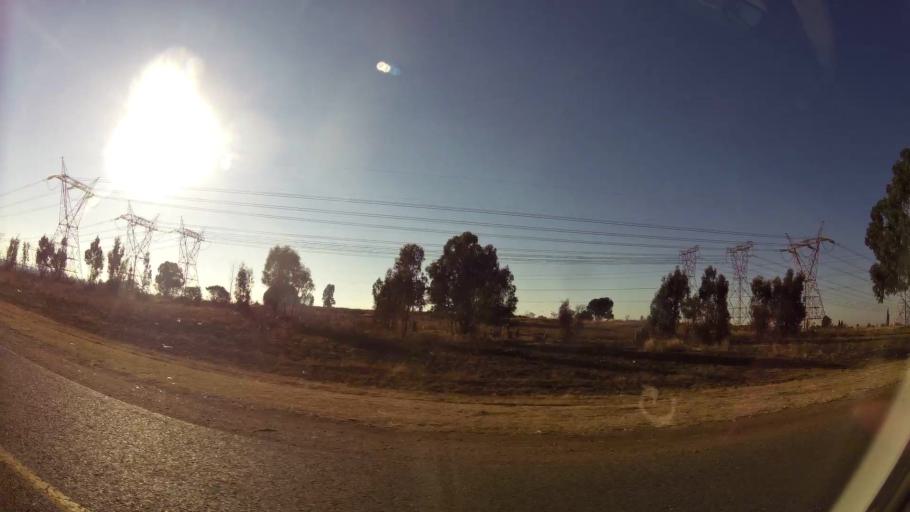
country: ZA
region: Gauteng
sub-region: Ekurhuleni Metropolitan Municipality
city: Germiston
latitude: -26.3136
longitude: 28.1126
